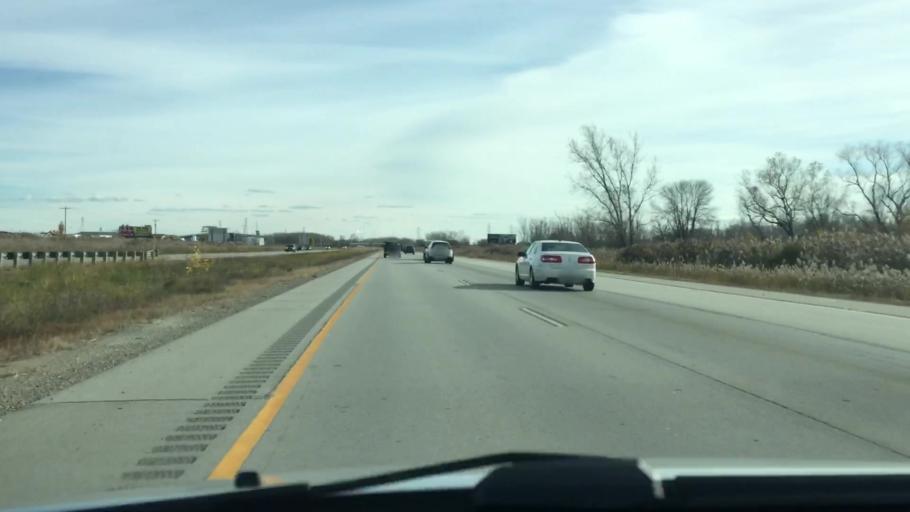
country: US
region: Wisconsin
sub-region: Brown County
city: Green Bay
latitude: 44.5477
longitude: -88.0362
